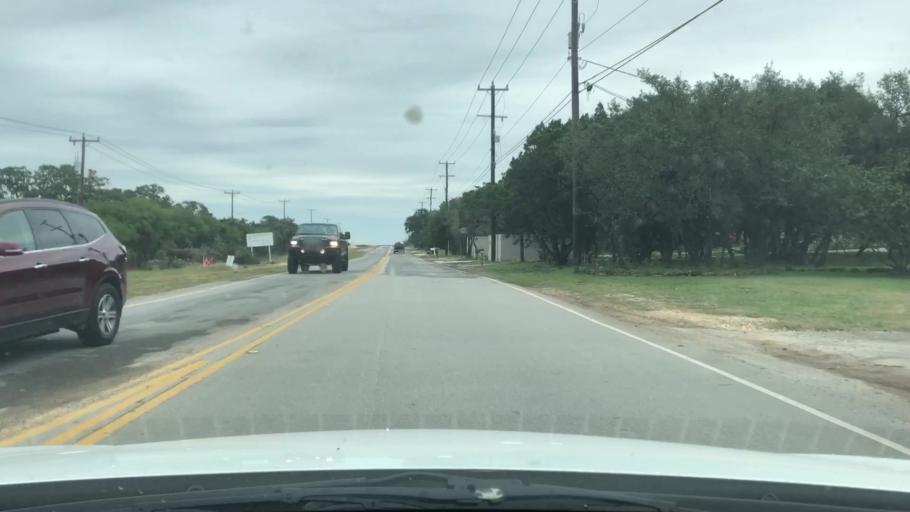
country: US
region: Texas
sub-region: Bexar County
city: Hollywood Park
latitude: 29.6478
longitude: -98.4231
